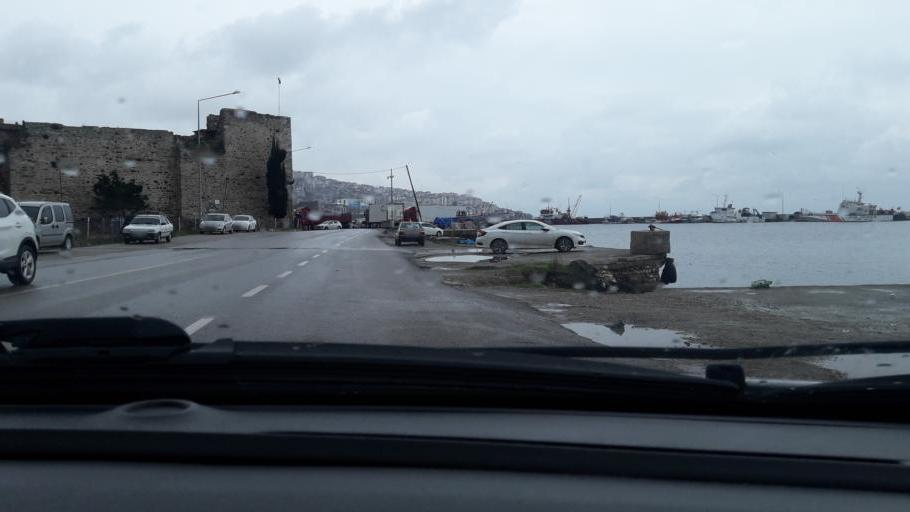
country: TR
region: Sinop
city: Sinop
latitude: 42.0237
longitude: 35.1419
